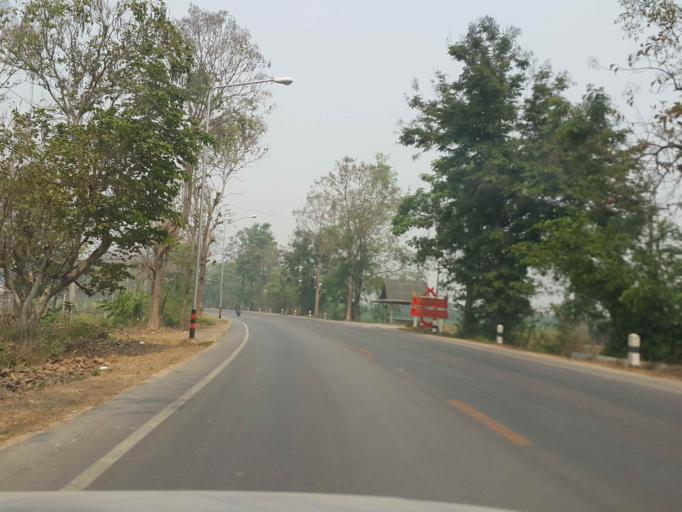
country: TH
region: Chiang Mai
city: Mae Taeng
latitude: 18.9978
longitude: 98.9767
